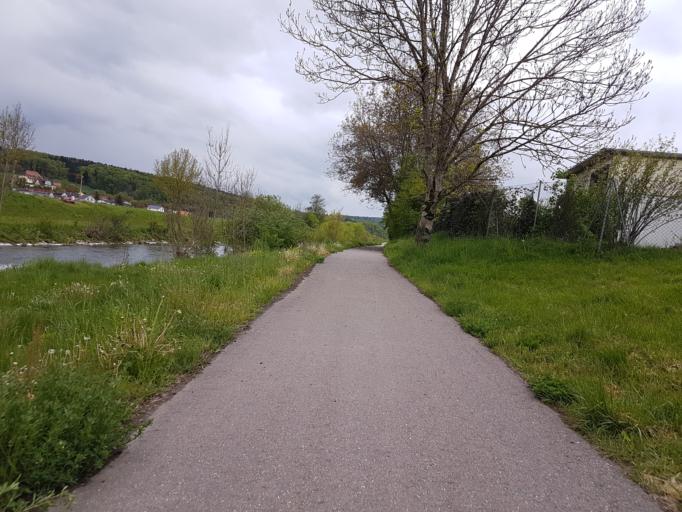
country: DE
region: Baden-Wuerttemberg
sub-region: Freiburg Region
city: Wutoschingen
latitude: 47.6458
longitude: 8.3516
